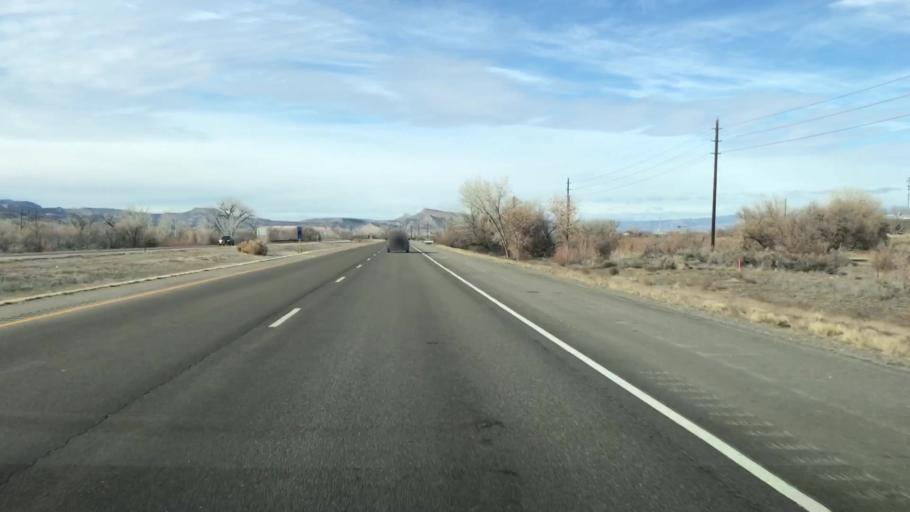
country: US
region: Colorado
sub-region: Mesa County
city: Fruita
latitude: 39.1594
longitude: -108.7545
